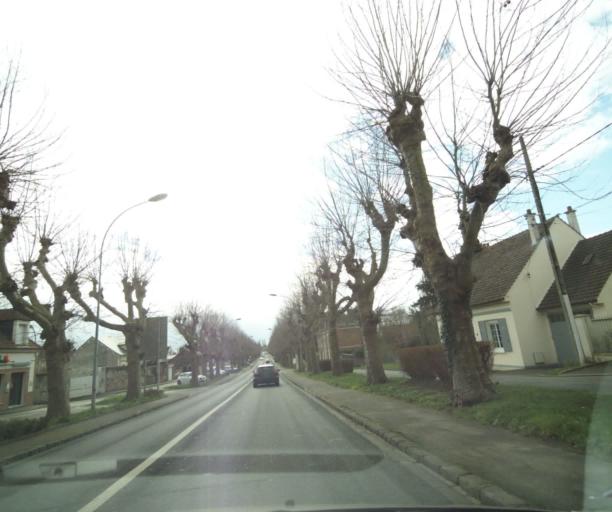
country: FR
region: Picardie
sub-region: Departement de l'Oise
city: Noyon
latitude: 49.5828
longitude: 2.9961
